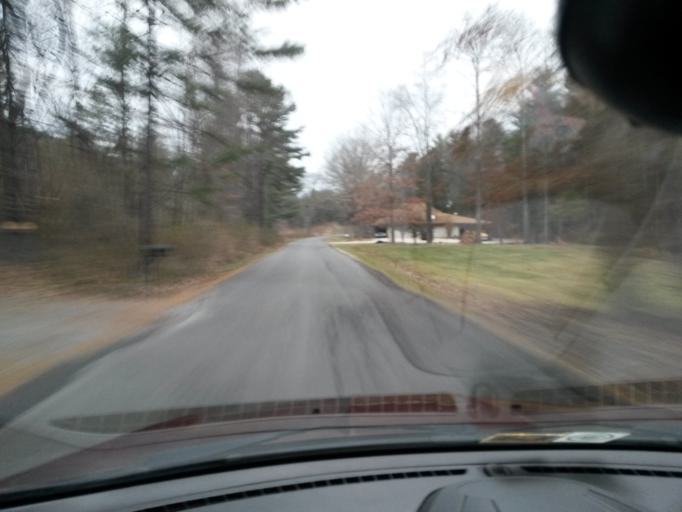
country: US
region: Virginia
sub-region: Bath County
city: Warm Springs
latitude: 37.9483
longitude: -79.7719
